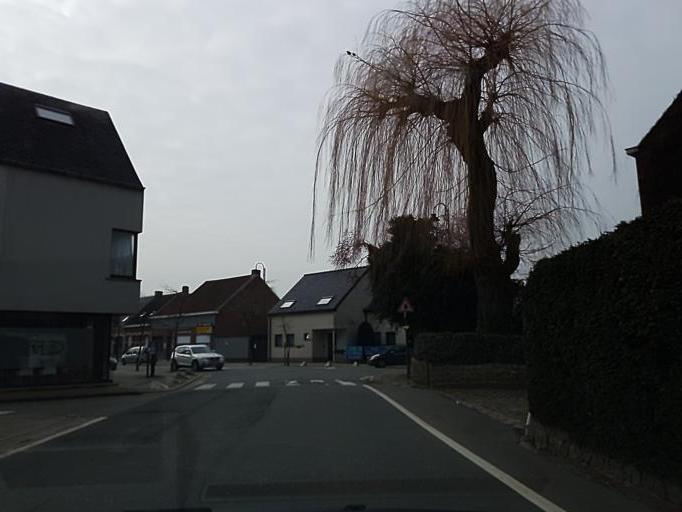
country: BE
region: Flanders
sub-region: Provincie Oost-Vlaanderen
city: Sint-Gillis-Waas
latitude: 51.2937
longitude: 4.1726
